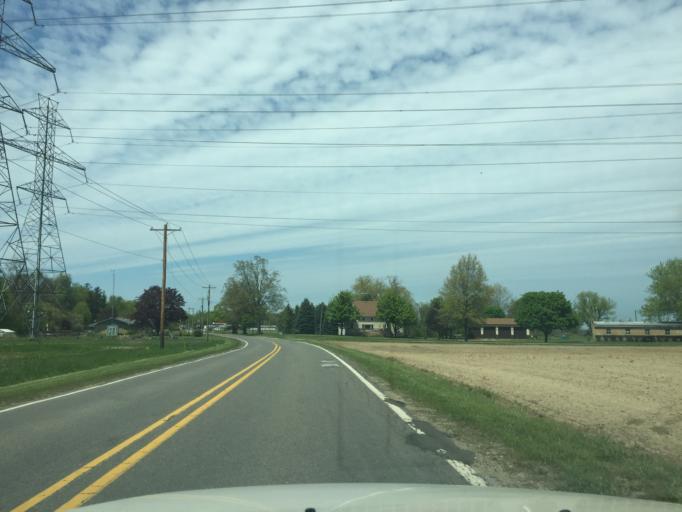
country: US
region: Michigan
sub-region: Berrien County
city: Stevensville
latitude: 41.9739
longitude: -86.4922
